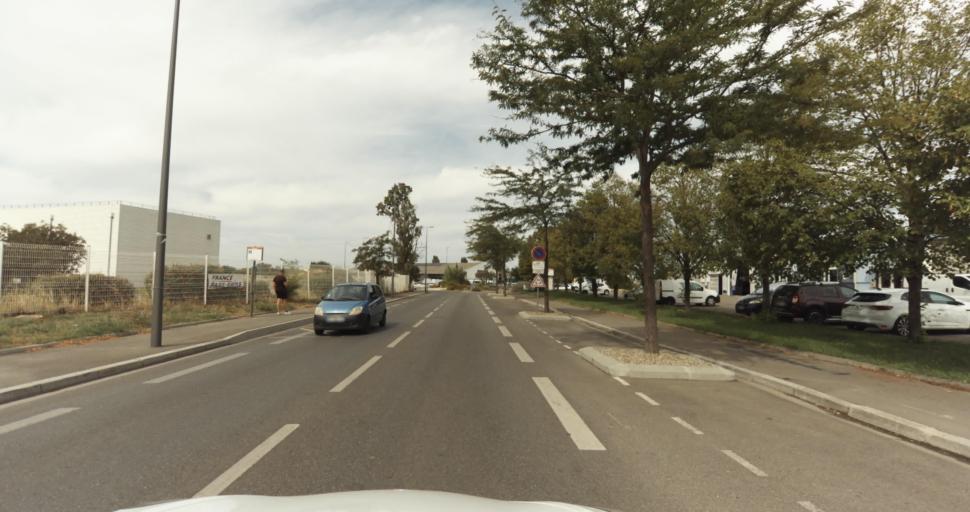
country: FR
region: Provence-Alpes-Cote d'Azur
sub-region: Departement des Bouches-du-Rhone
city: Miramas
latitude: 43.5990
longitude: 5.0030
